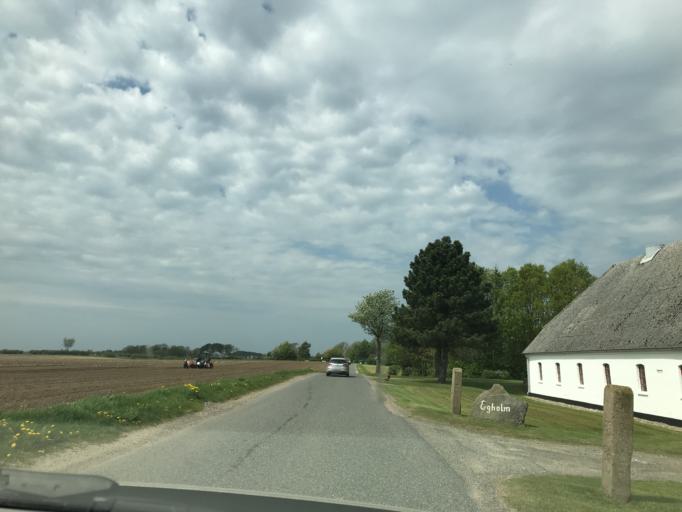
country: DK
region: South Denmark
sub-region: Assens Kommune
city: Assens
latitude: 55.3272
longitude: 9.9047
